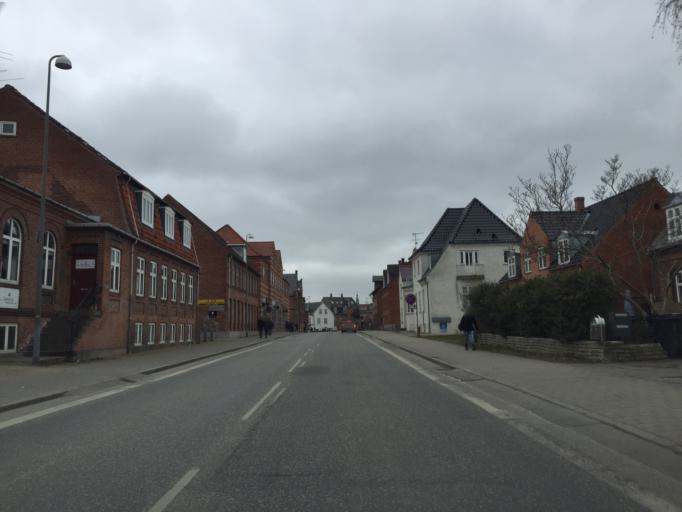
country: DK
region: Capital Region
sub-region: Hillerod Kommune
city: Hillerod
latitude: 55.9297
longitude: 12.3091
